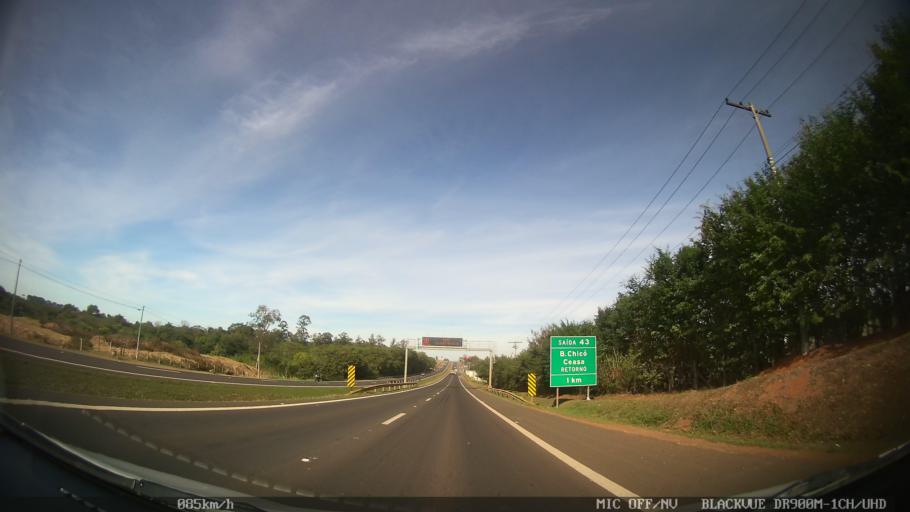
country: BR
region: Sao Paulo
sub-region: Piracicaba
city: Piracicaba
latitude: -22.7709
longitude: -47.6480
